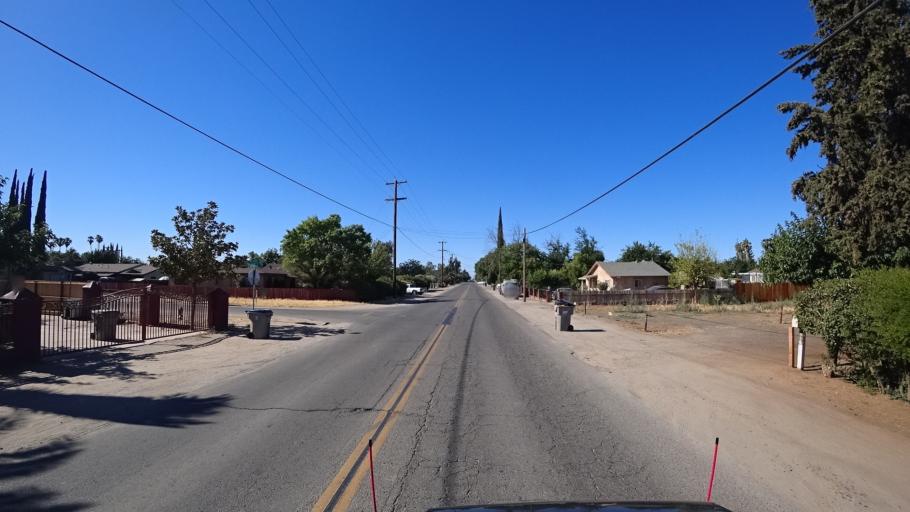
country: US
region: California
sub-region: Fresno County
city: West Park
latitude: 36.7555
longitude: -119.8356
